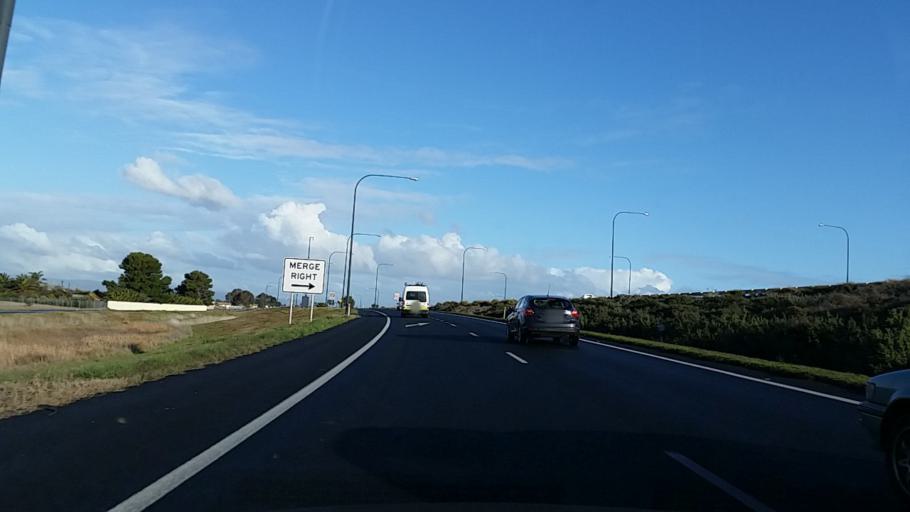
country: AU
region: South Australia
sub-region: Playford
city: Virginia
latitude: -34.7060
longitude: 138.5737
